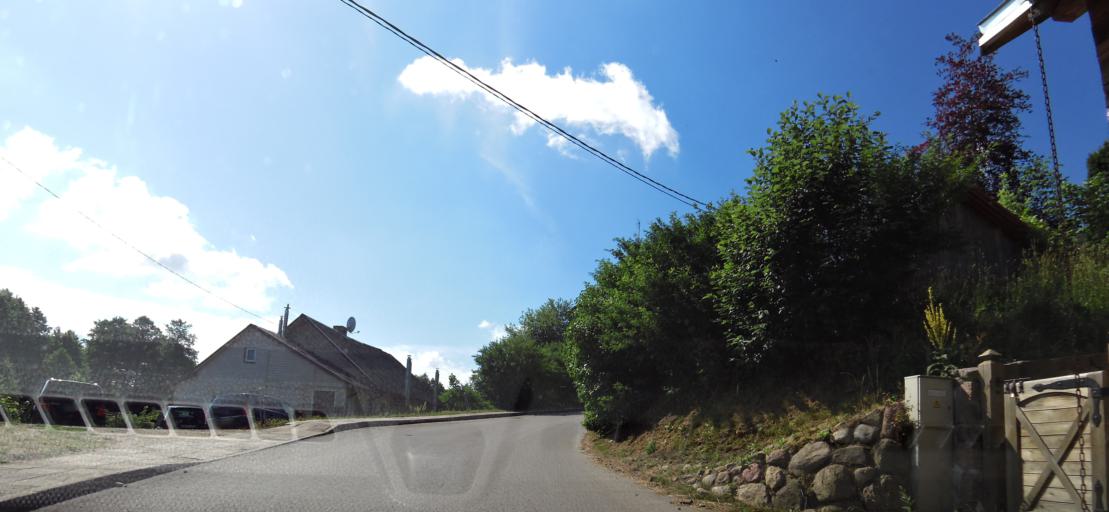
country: LT
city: Nemencine
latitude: 54.7960
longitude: 25.3977
